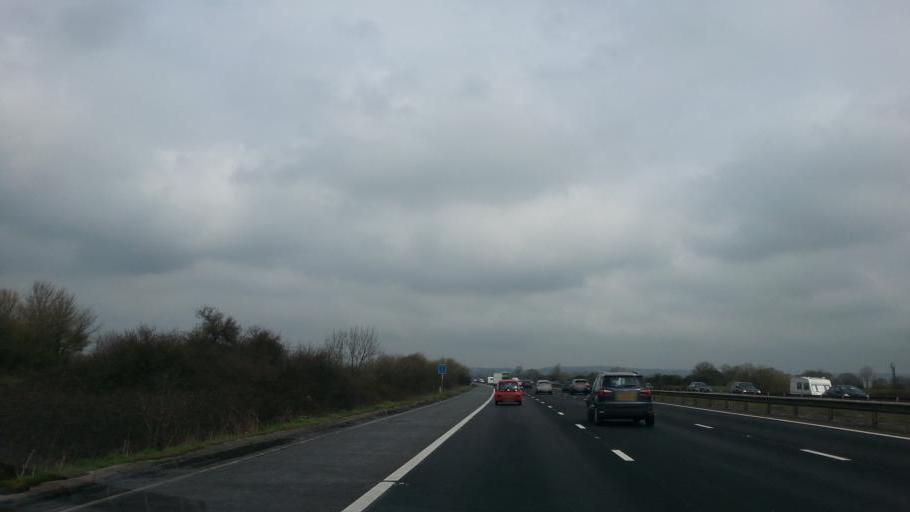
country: GB
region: England
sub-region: North Somerset
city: Kingston Seymour
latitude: 51.4026
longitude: -2.8538
